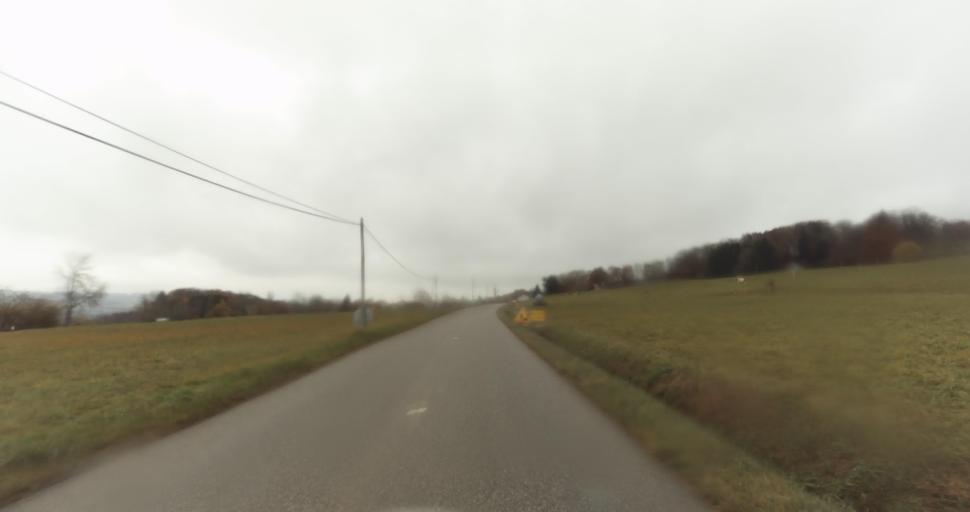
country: FR
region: Rhone-Alpes
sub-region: Departement de la Haute-Savoie
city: Thorens-Glieres
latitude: 46.0126
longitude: 6.2399
